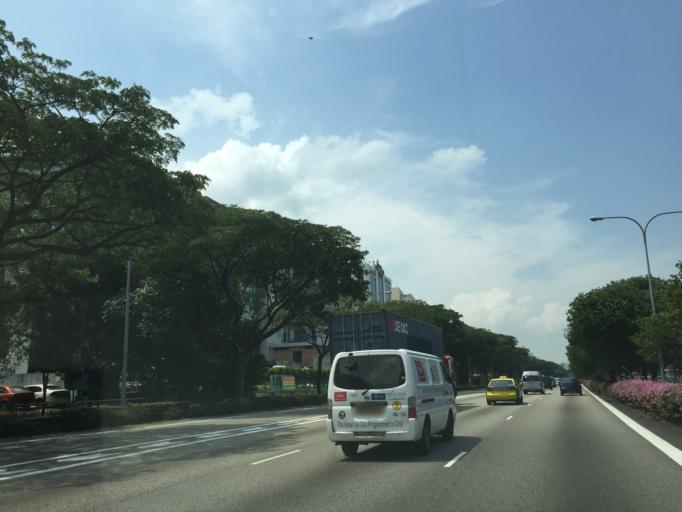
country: SG
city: Singapore
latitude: 1.3237
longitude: 103.8940
